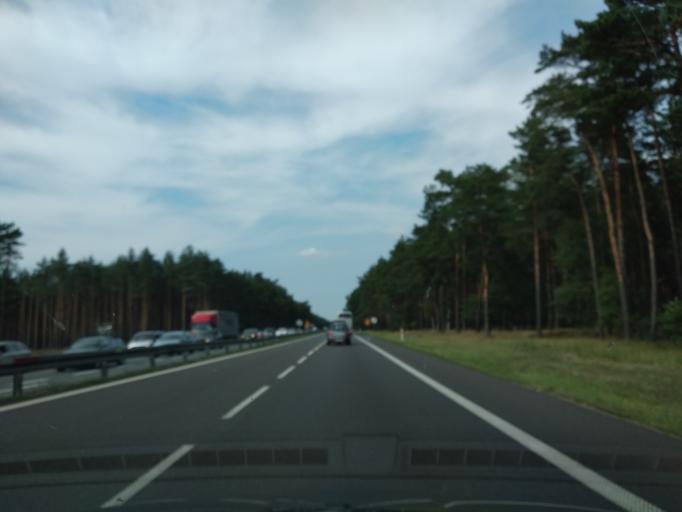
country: PL
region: West Pomeranian Voivodeship
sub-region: Powiat stargardzki
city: Kobylanka
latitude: 53.4276
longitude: 14.7719
